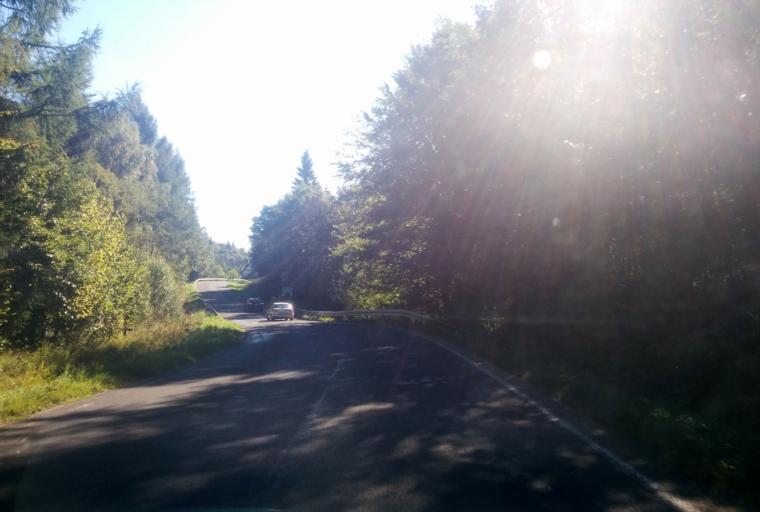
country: PL
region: Subcarpathian Voivodeship
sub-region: Powiat leski
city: Cisna
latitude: 49.1905
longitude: 22.3787
